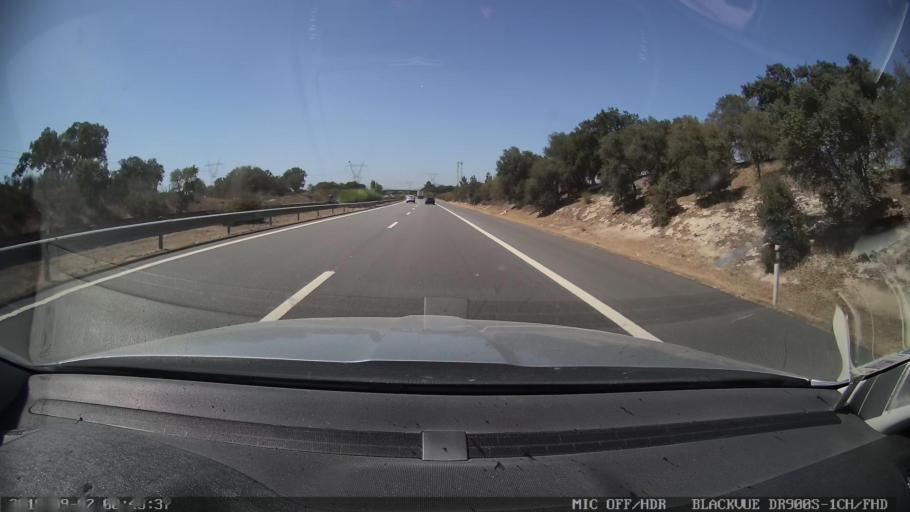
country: PT
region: Setubal
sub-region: Palmela
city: Palmela
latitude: 38.5873
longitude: -8.7671
